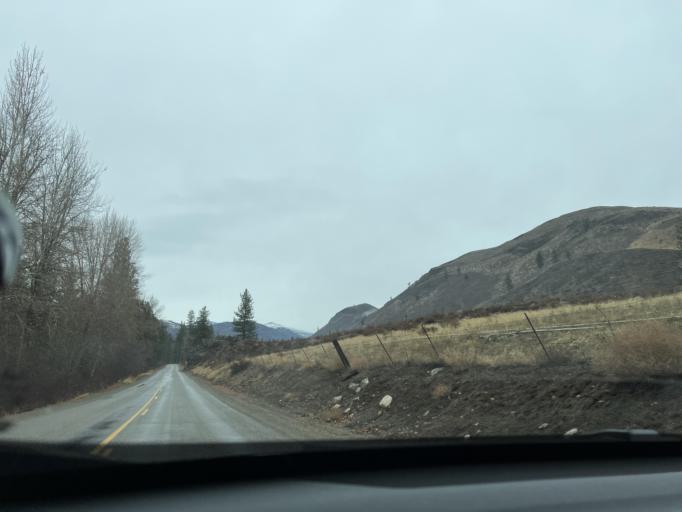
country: US
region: Washington
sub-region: Okanogan County
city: Brewster
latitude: 48.5259
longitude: -120.1794
